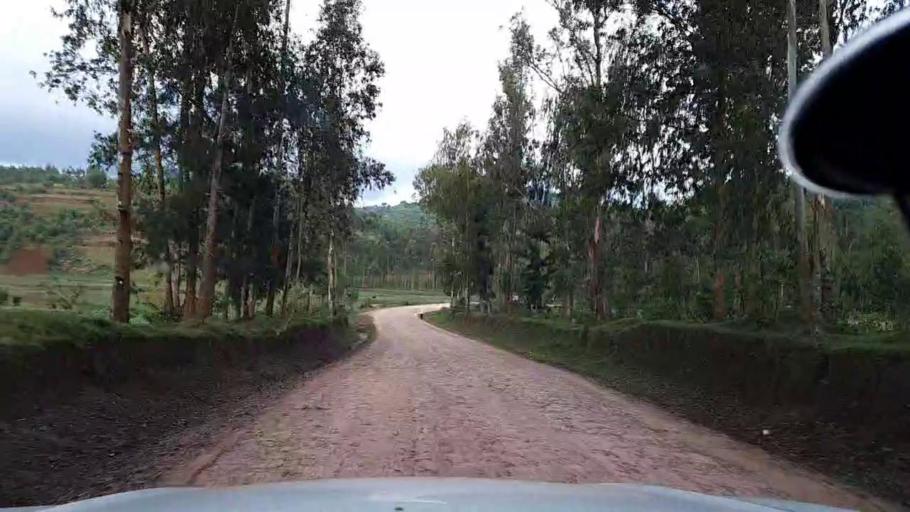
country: RW
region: Southern Province
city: Gitarama
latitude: -2.2095
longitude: 29.6155
